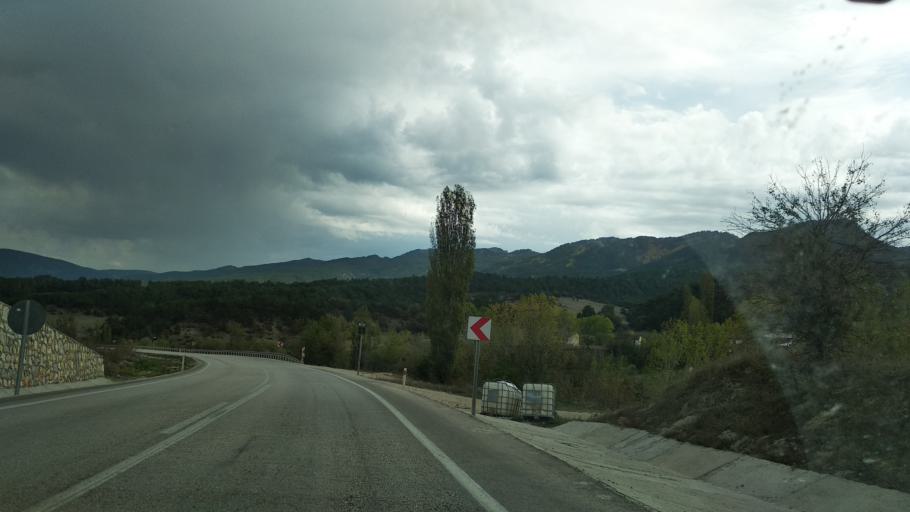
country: TR
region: Bolu
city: Mudurnu
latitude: 40.4368
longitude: 31.1559
